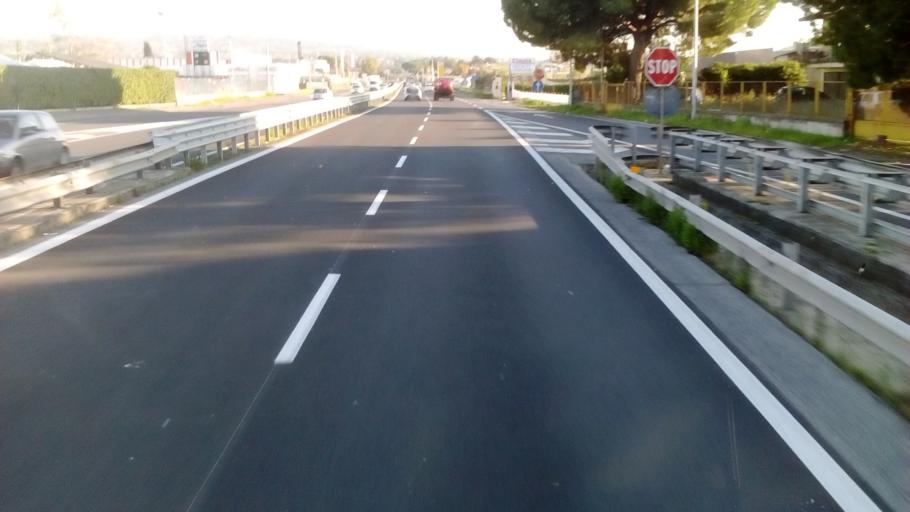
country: IT
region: Latium
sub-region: Citta metropolitana di Roma Capitale
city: Ciampino
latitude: 41.7856
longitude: 12.5987
